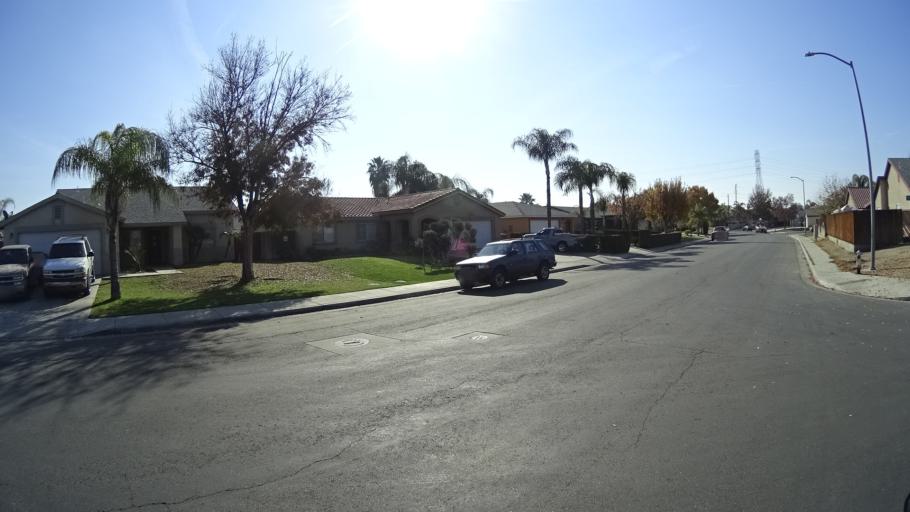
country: US
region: California
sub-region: Kern County
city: Greenfield
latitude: 35.3151
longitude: -119.0258
